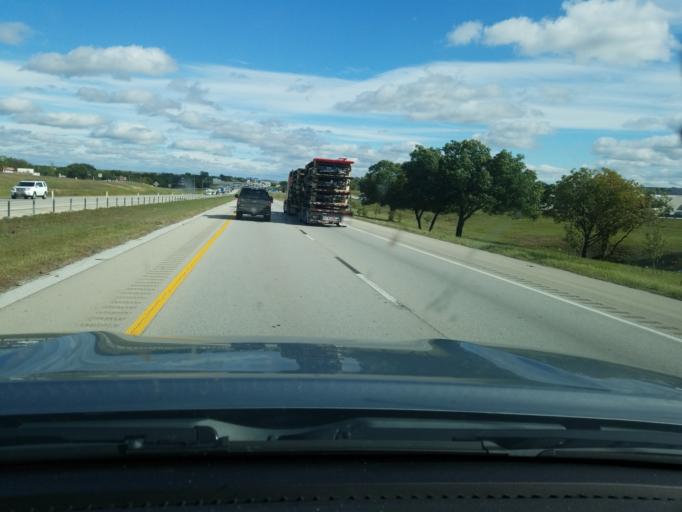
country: US
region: Texas
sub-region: Parker County
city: Hudson Oaks
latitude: 32.7538
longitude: -97.6923
